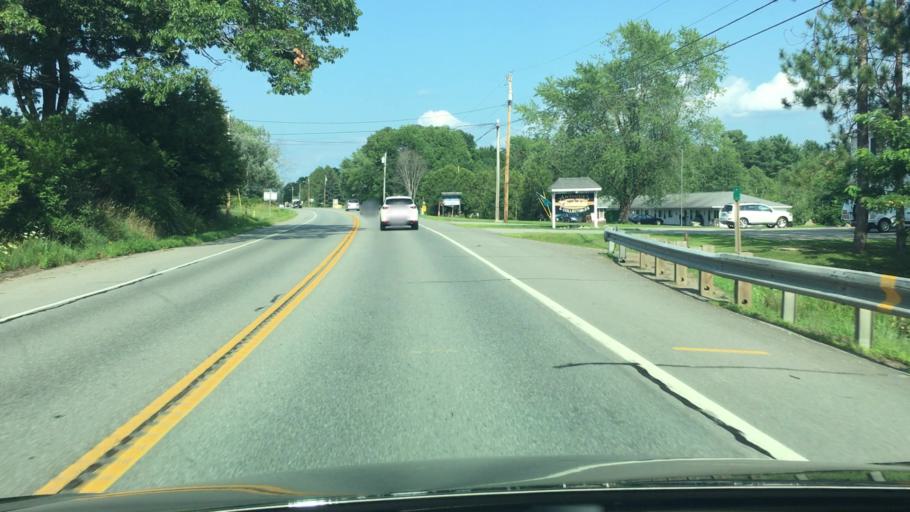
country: US
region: Maine
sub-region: Kennebec County
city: Windsor
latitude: 44.3862
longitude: -69.5982
